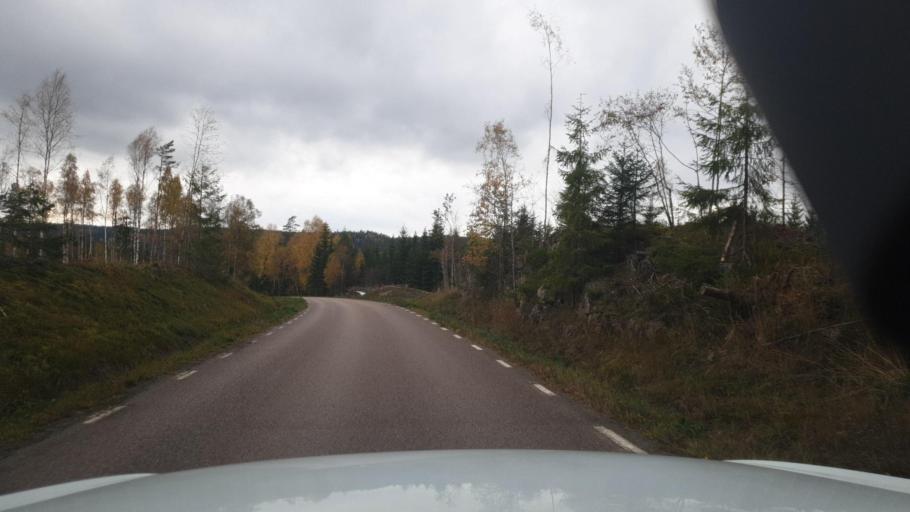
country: SE
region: Vaermland
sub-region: Sunne Kommun
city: Sunne
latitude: 59.8259
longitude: 12.8485
